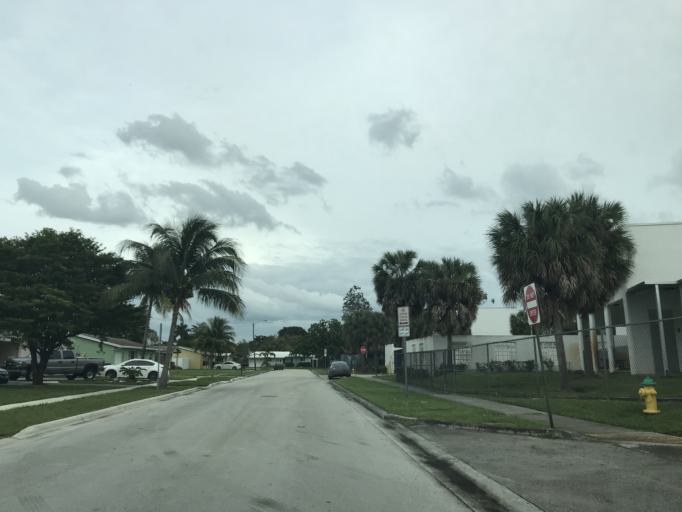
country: US
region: Florida
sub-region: Broward County
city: Margate
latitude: 26.2517
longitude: -80.2101
